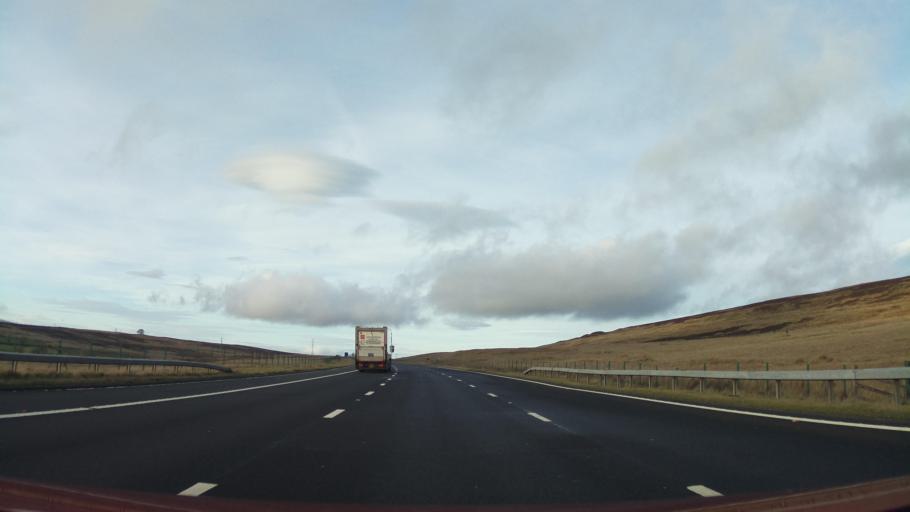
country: GB
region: England
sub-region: Cumbria
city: Appleby-in-Westmorland
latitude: 54.4850
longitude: -2.6372
